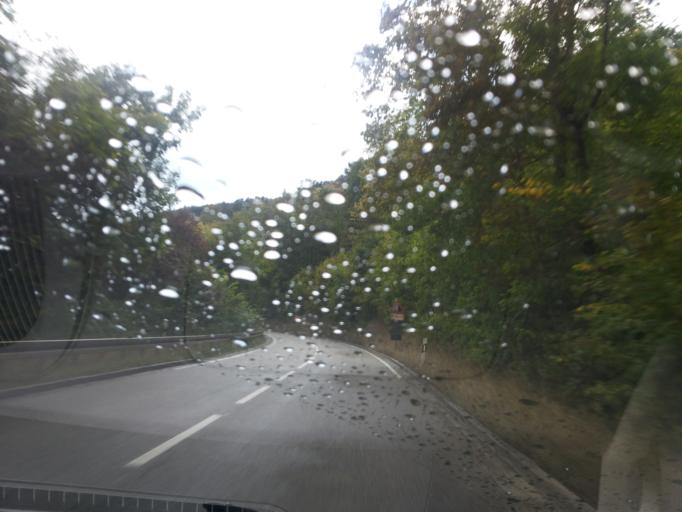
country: DE
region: Bavaria
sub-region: Upper Bavaria
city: Eichstaett
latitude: 48.9023
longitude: 11.1734
